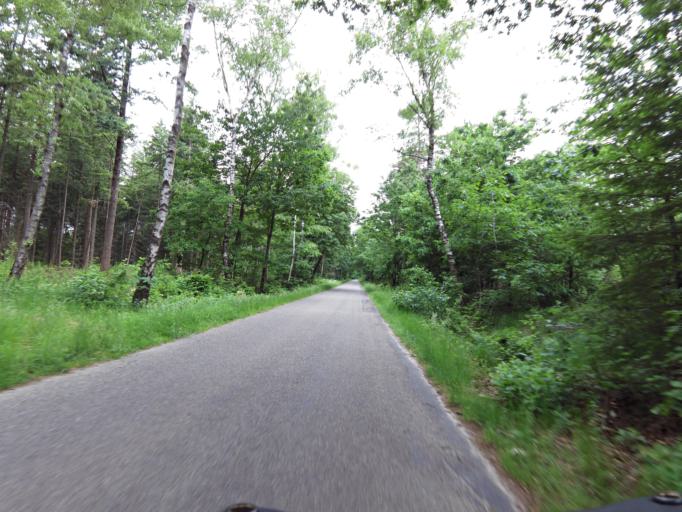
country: NL
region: North Brabant
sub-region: Gemeente Breda
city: Breda
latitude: 51.5382
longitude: 4.8579
